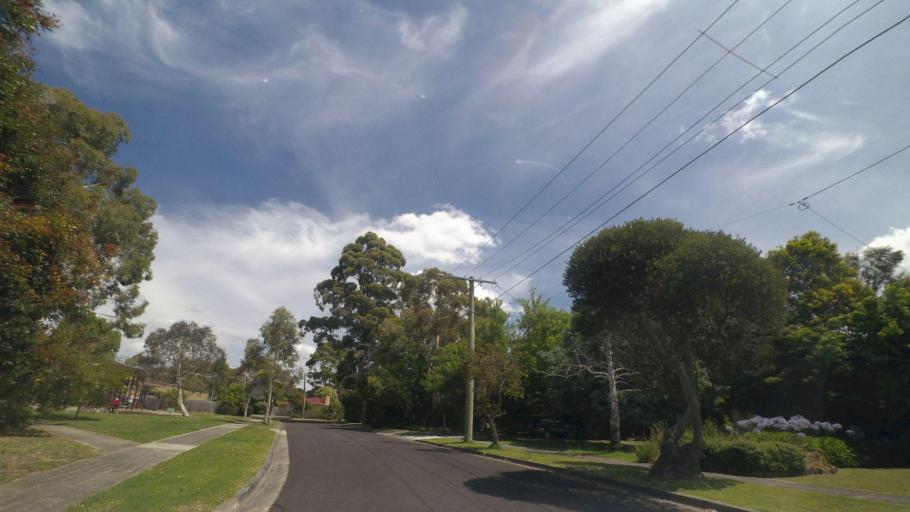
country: AU
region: Victoria
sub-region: Maroondah
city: Bayswater North
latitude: -37.8422
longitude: 145.2937
